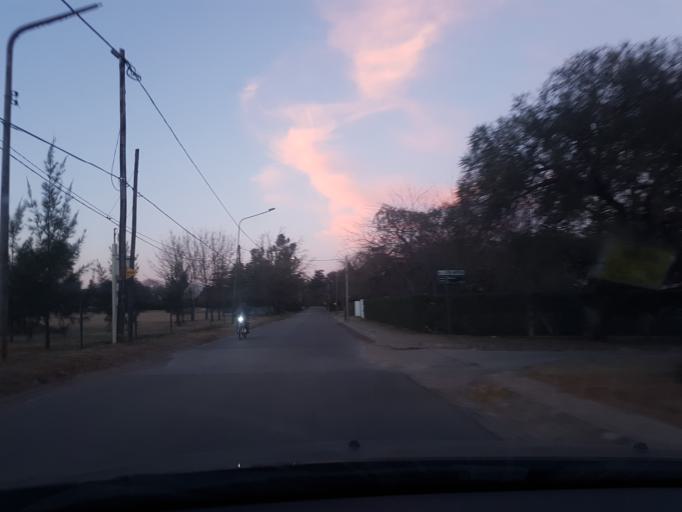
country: AR
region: Cordoba
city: Villa Allende
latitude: -31.2817
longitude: -64.2870
